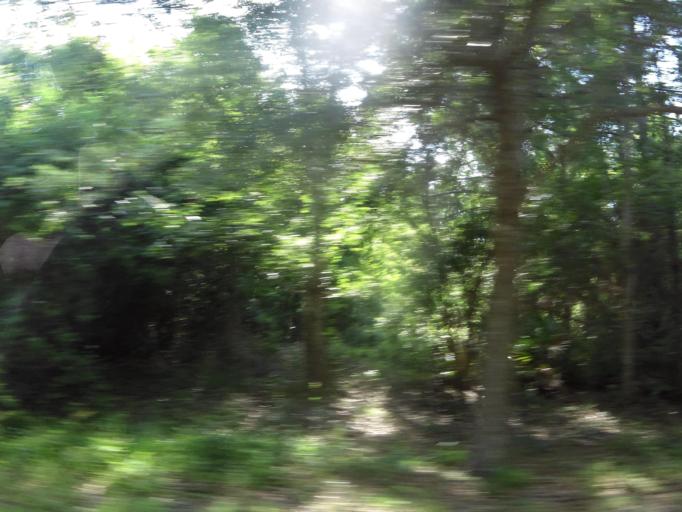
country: US
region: Florida
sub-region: Nassau County
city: Fernandina Beach
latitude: 30.4909
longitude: -81.4910
